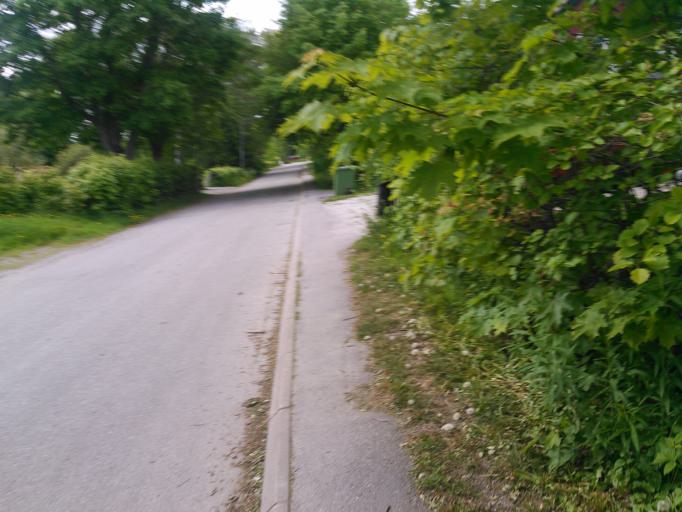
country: SE
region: Vaesterbotten
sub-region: Umea Kommun
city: Umea
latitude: 63.8233
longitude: 20.2439
